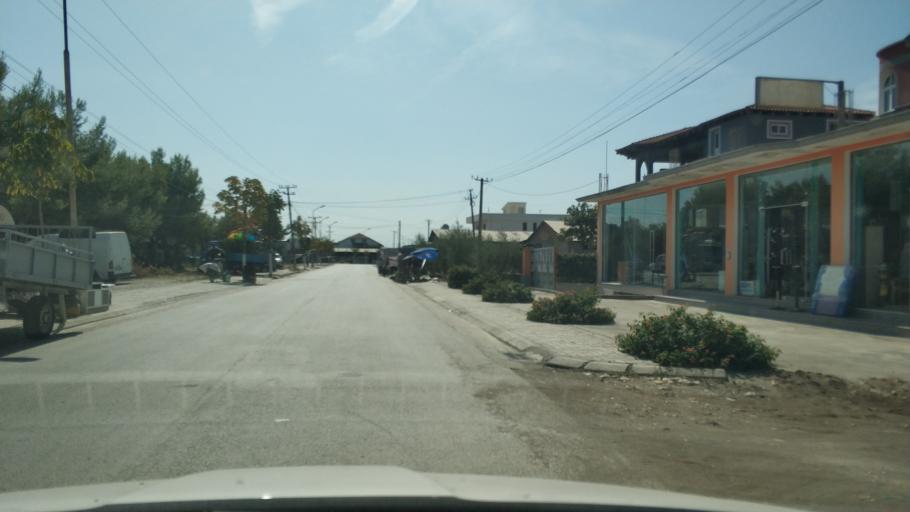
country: AL
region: Fier
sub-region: Rrethi i Lushnjes
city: Divjake
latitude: 40.9933
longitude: 19.5334
